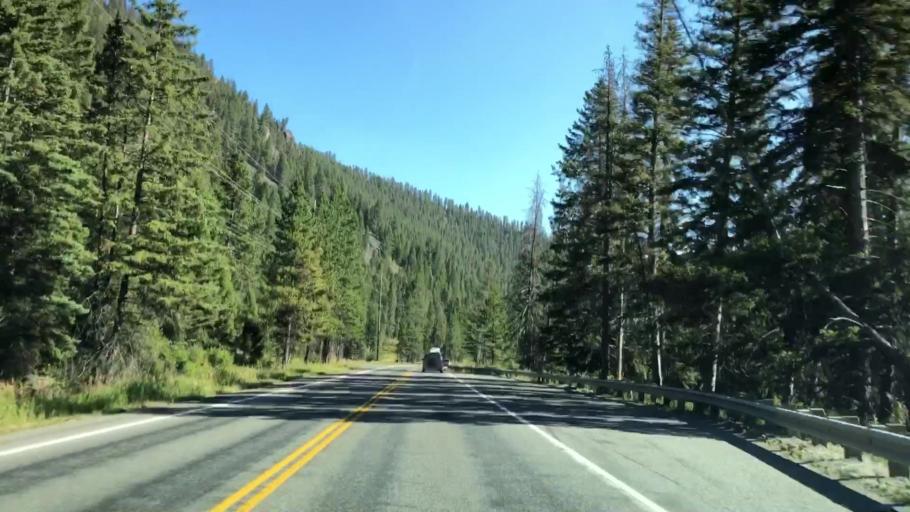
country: US
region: Montana
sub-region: Gallatin County
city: Big Sky
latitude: 45.3639
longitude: -111.1734
